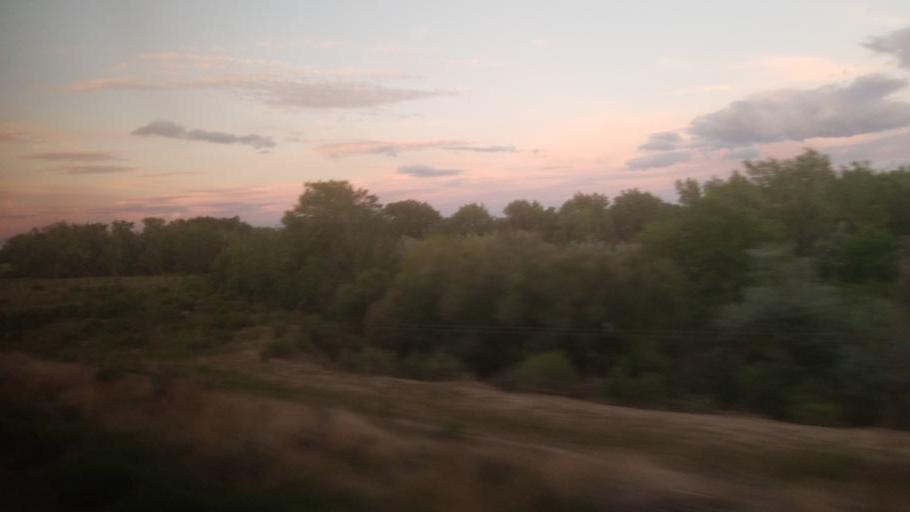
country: US
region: Colorado
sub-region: Las Animas County
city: Trinidad
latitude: 37.2421
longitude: -104.4244
